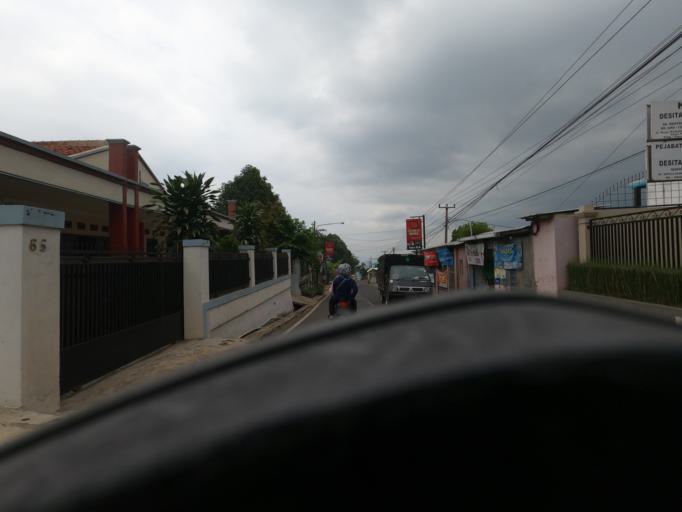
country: ID
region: West Java
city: Cimahi
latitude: -6.8291
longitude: 107.5226
